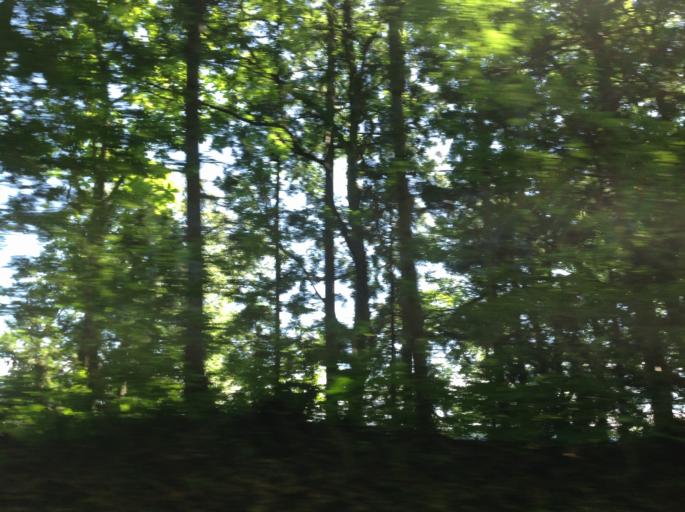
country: JP
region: Akita
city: Kakunodatemachi
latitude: 39.6995
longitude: 140.6475
